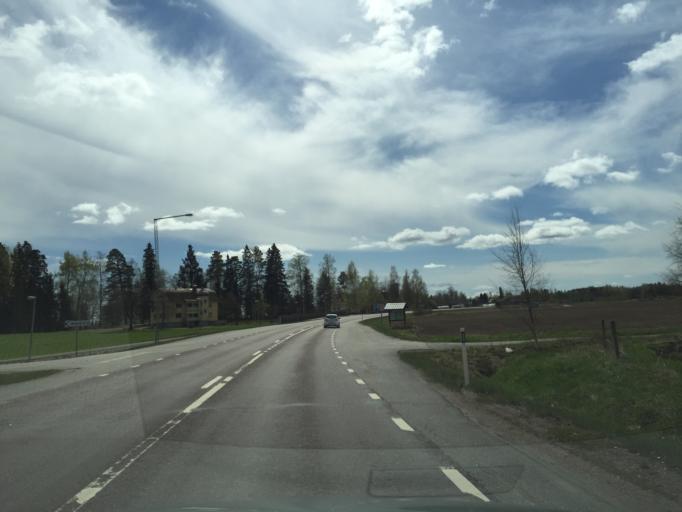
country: SE
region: Gaevleborg
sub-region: Bollnas Kommun
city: Arbra
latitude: 61.4912
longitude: 16.3743
